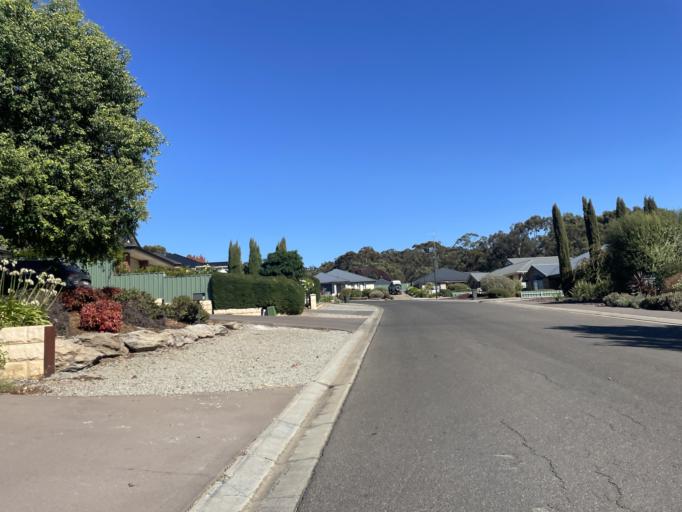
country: AU
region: South Australia
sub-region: Clare and Gilbert Valleys
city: Clare
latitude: -33.8449
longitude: 138.6109
